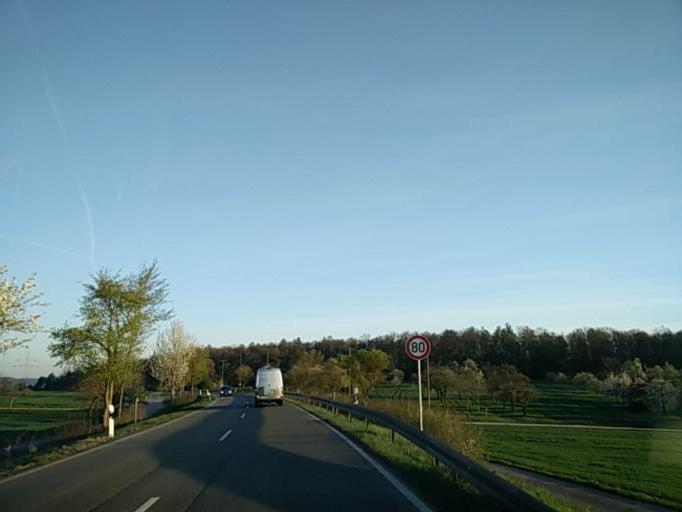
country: DE
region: Baden-Wuerttemberg
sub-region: Regierungsbezirk Stuttgart
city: Hildrizhausen
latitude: 48.6318
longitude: 8.9571
